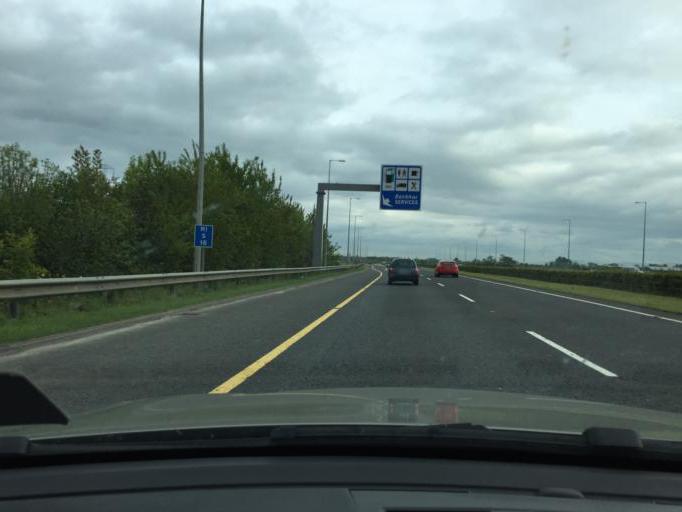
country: IE
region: Leinster
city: Lusk
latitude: 53.5433
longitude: -6.2138
